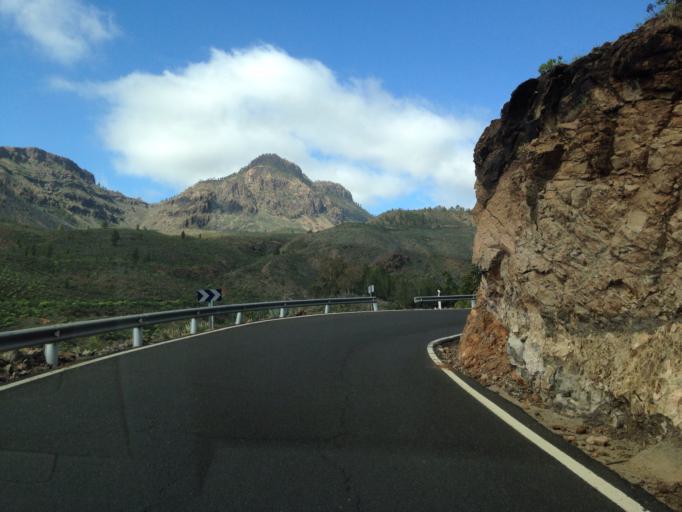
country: ES
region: Canary Islands
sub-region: Provincia de Las Palmas
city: Santa Lucia
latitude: 27.8953
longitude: -15.5631
